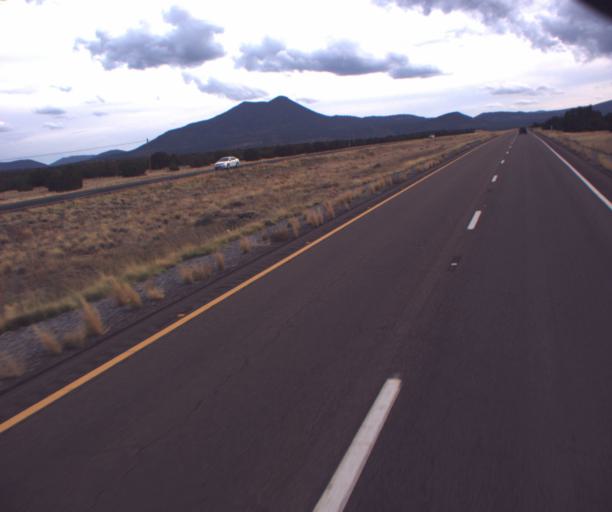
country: US
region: Arizona
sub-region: Coconino County
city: Flagstaff
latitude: 35.4804
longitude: -111.5568
